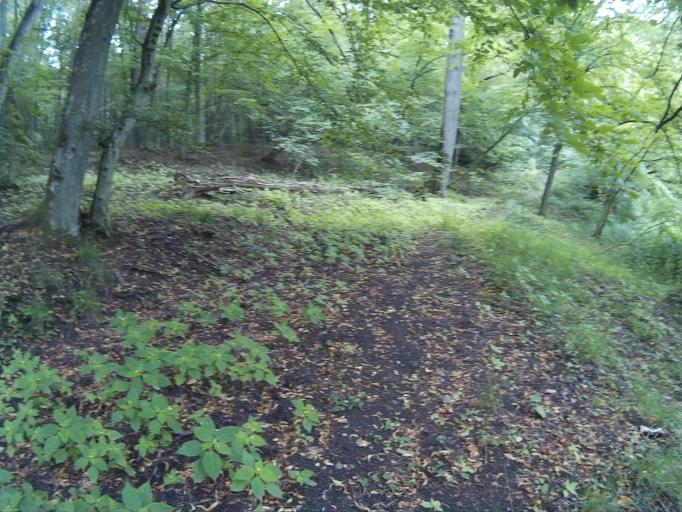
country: PL
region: Kujawsko-Pomorskie
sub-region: Powiat tucholski
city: Tuchola
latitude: 53.5300
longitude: 17.8766
